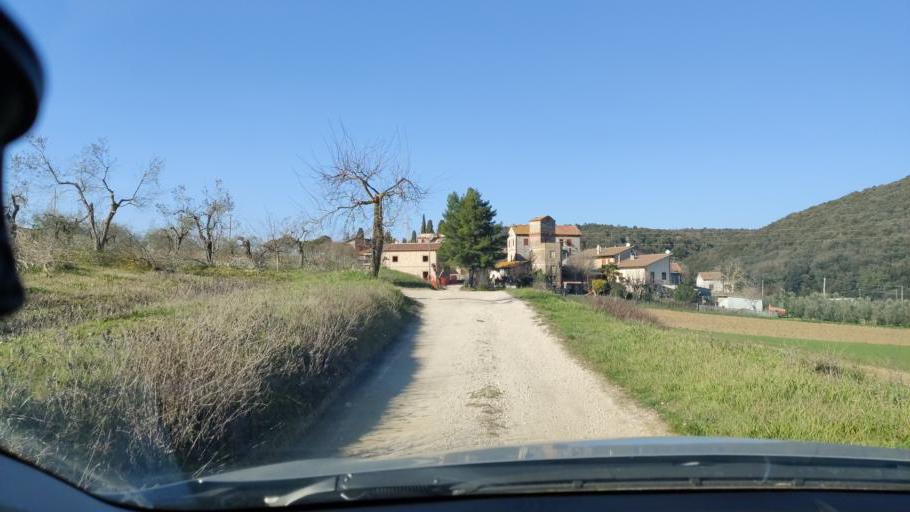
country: IT
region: Umbria
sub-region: Provincia di Terni
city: Fornole
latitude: 42.5615
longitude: 12.4491
